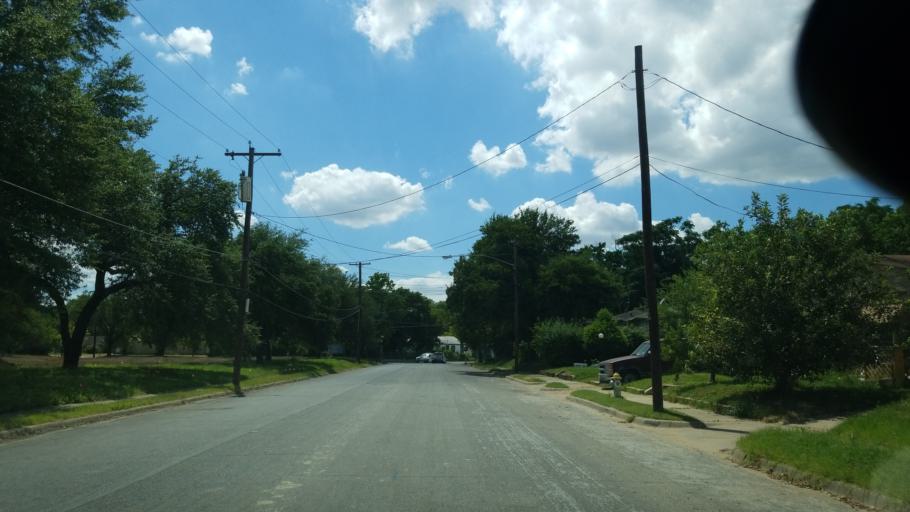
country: US
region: Texas
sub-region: Dallas County
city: Dallas
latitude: 32.7464
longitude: -96.7520
